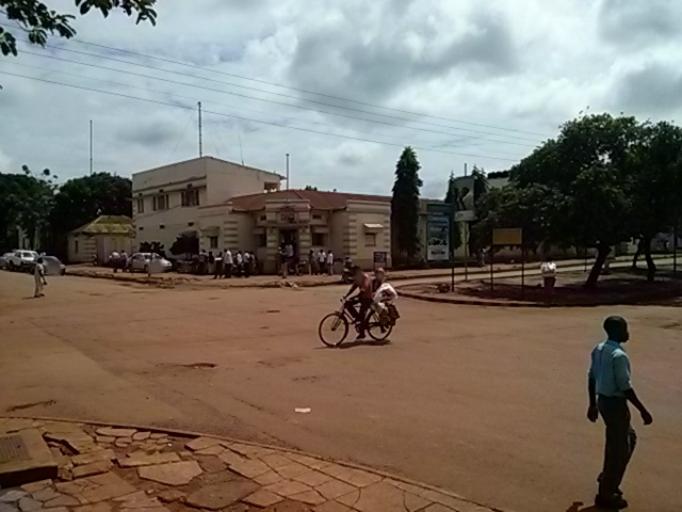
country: UG
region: Eastern Region
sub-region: Jinja District
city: Jinja
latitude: 0.4737
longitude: 33.1586
